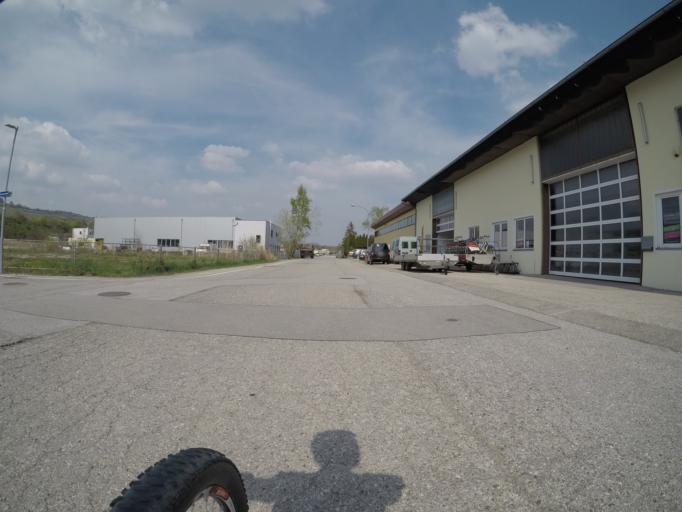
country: AT
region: Lower Austria
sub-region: Politischer Bezirk Modling
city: Guntramsdorf
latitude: 48.0536
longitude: 16.3068
